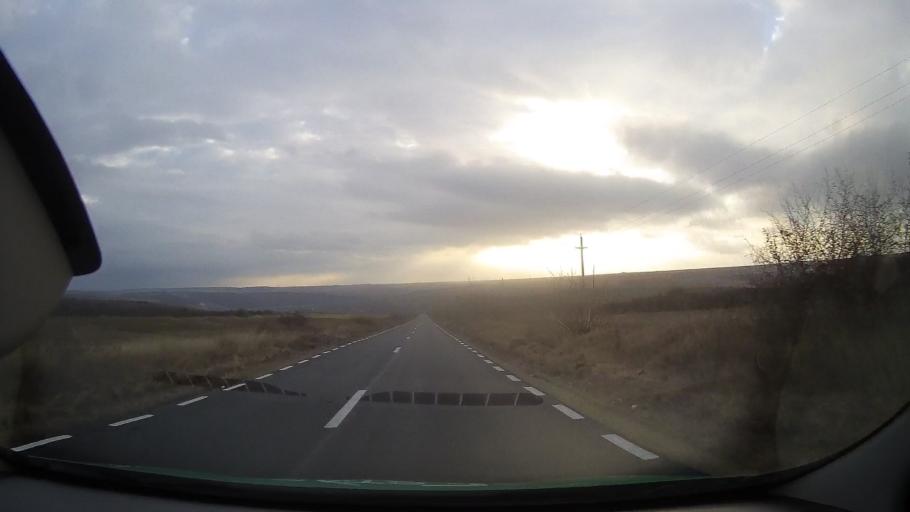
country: RO
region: Constanta
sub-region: Comuna Adamclisi
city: Adamclisi
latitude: 44.0637
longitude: 27.9714
